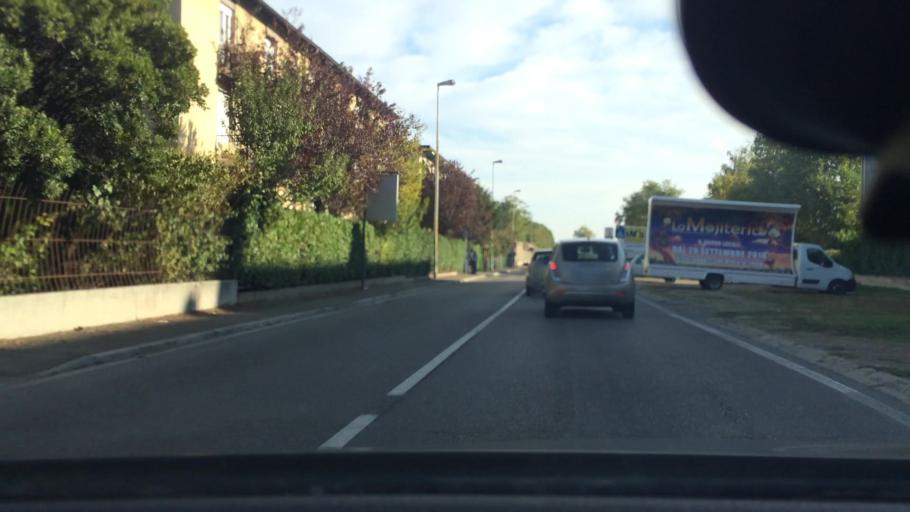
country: IT
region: Lombardy
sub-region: Citta metropolitana di Milano
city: Legnano
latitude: 45.5875
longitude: 8.9022
